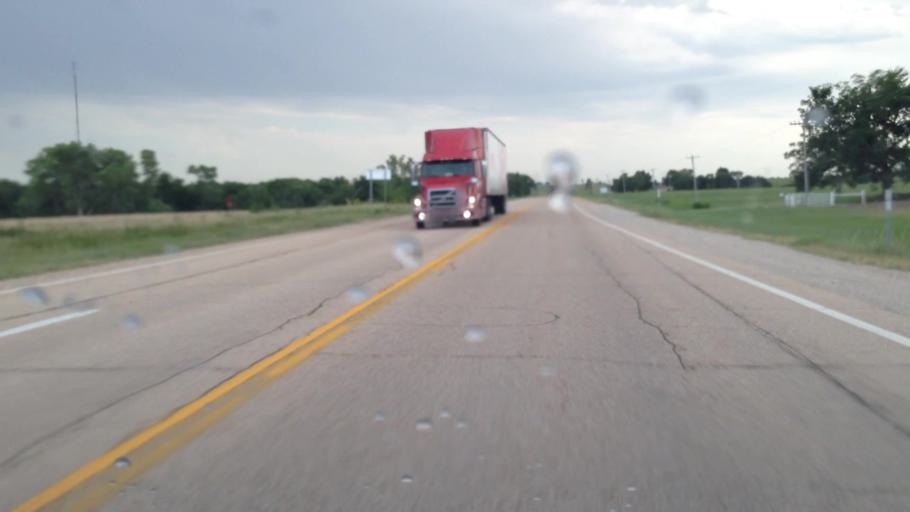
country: US
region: Kansas
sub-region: Coffey County
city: Burlington
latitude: 38.1699
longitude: -95.7389
